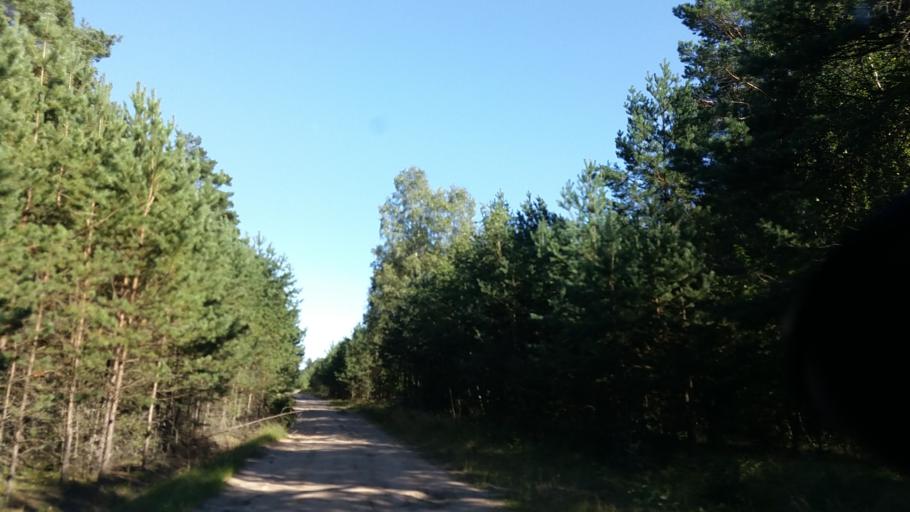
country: PL
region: West Pomeranian Voivodeship
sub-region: Powiat szczecinecki
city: Borne Sulinowo
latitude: 53.5559
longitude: 16.5071
